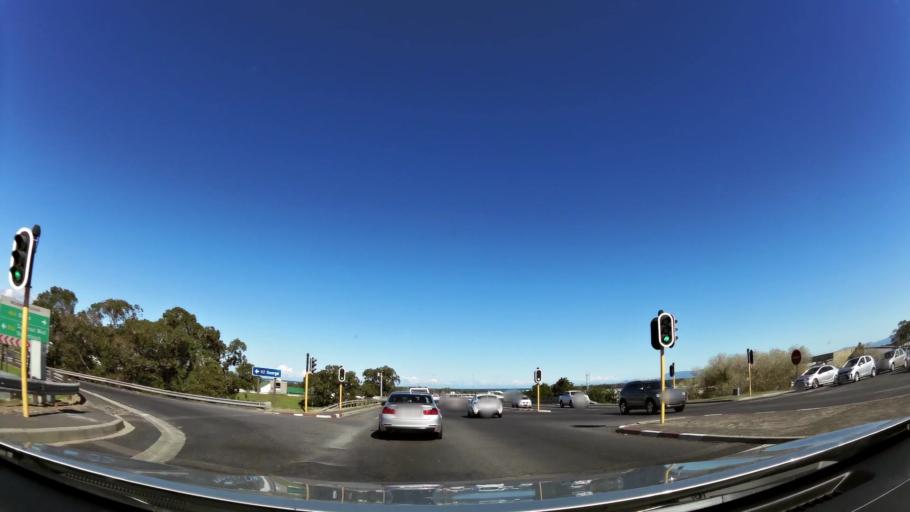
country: ZA
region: Western Cape
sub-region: Cape Winelands District Municipality
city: Stellenbosch
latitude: -34.0763
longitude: 18.8217
